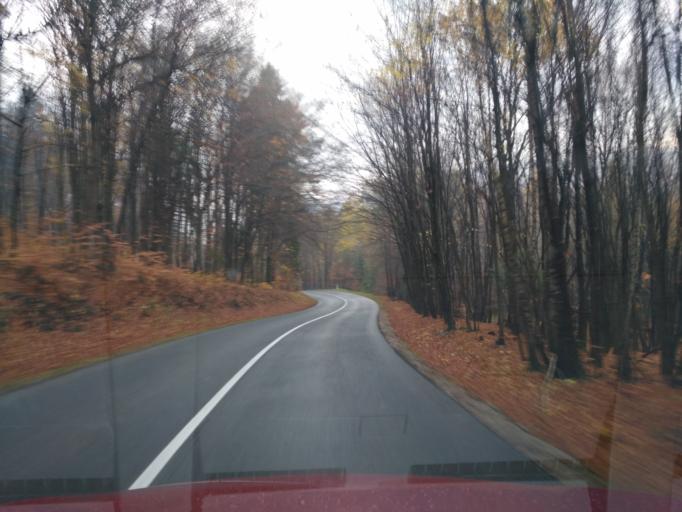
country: SK
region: Kosicky
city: Medzev
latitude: 48.7036
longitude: 20.8292
